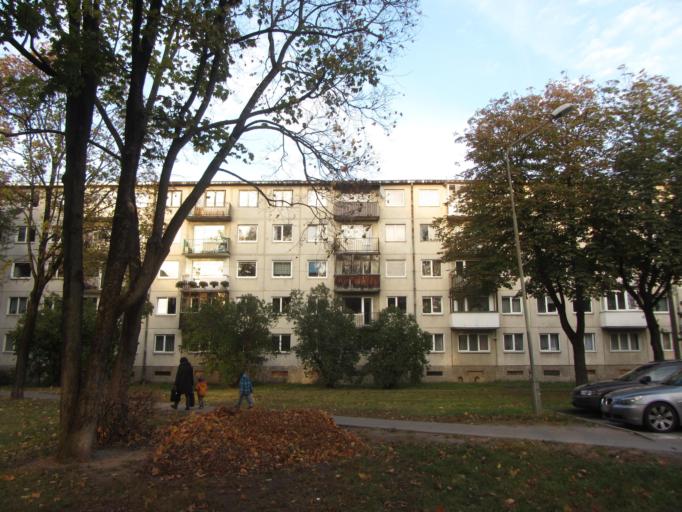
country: LT
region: Vilnius County
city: Vilkpede
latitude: 54.6744
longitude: 25.2469
